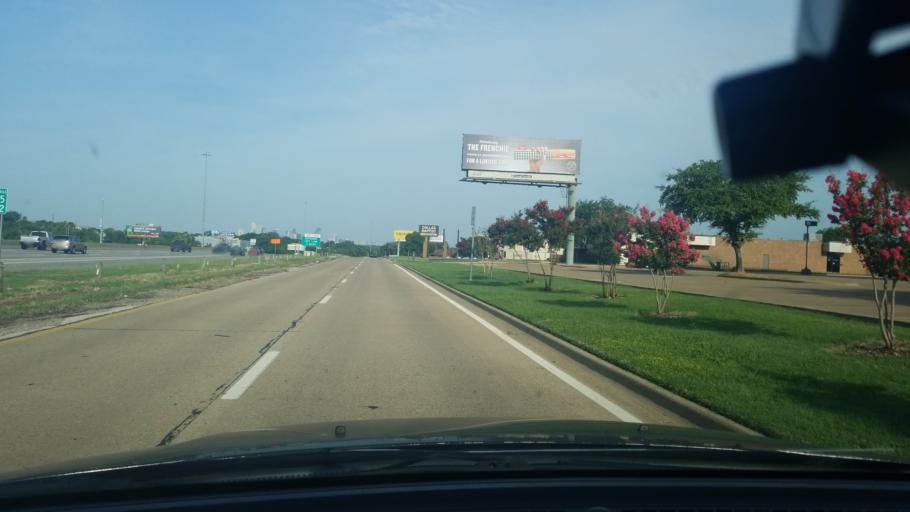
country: US
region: Texas
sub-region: Dallas County
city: Highland Park
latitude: 32.7943
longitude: -96.7037
